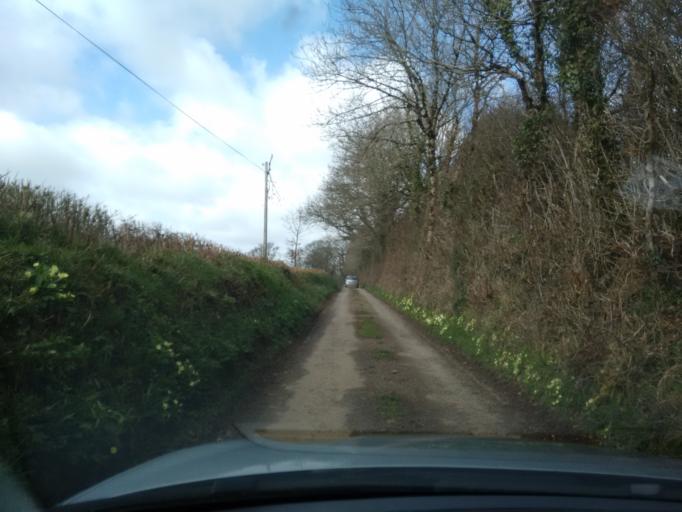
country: GB
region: England
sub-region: Cornwall
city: Launceston
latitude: 50.5993
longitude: -4.3131
